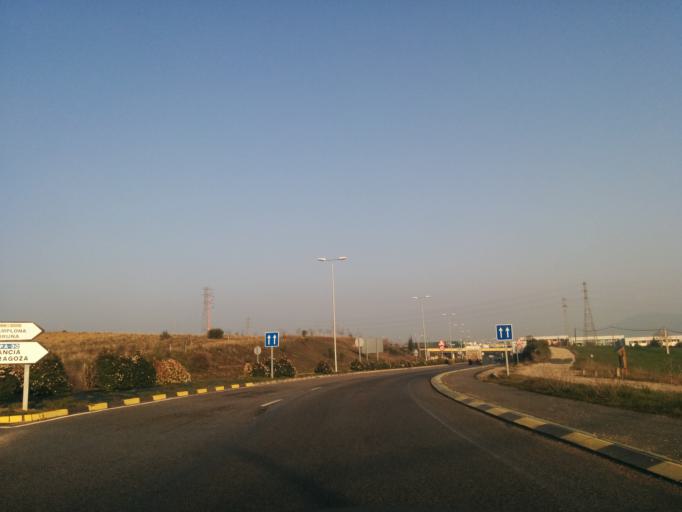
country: ES
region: Navarre
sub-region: Provincia de Navarra
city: Segundo Ensanche
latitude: 42.7791
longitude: -1.6178
